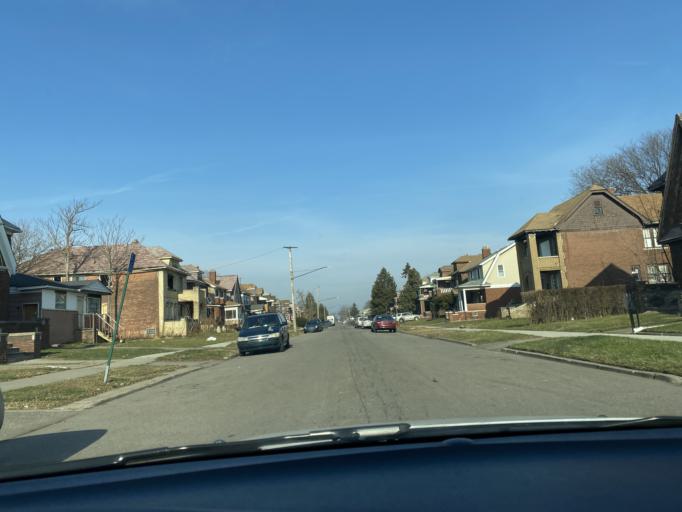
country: US
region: Michigan
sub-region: Wayne County
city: Highland Park
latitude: 42.3767
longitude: -83.1413
